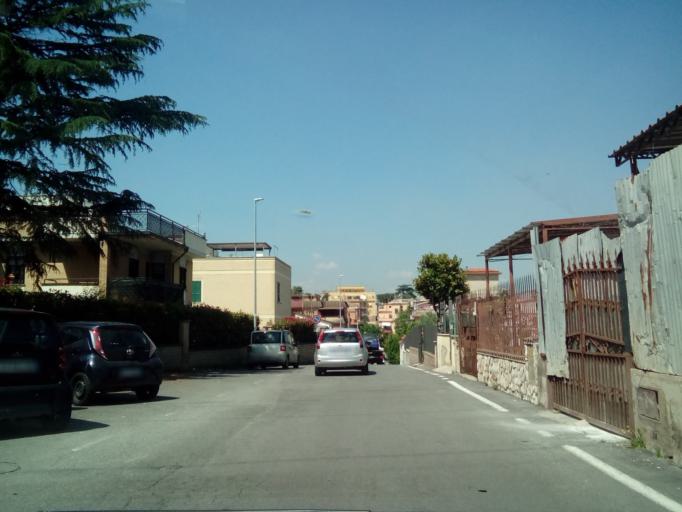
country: IT
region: Latium
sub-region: Citta metropolitana di Roma Capitale
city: Rome
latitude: 41.8789
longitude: 12.5839
